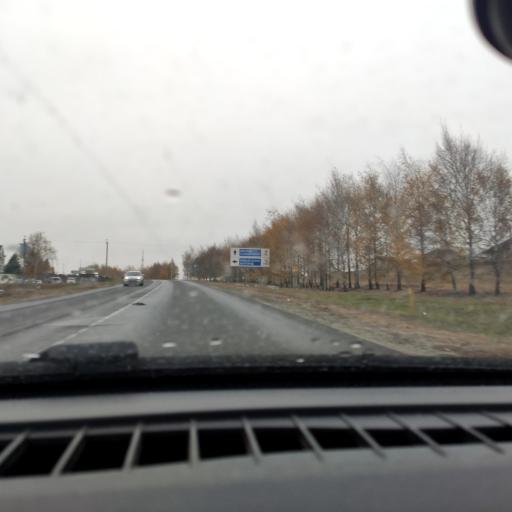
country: RU
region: Belgorod
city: Alekseyevka
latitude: 50.6440
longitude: 38.6868
